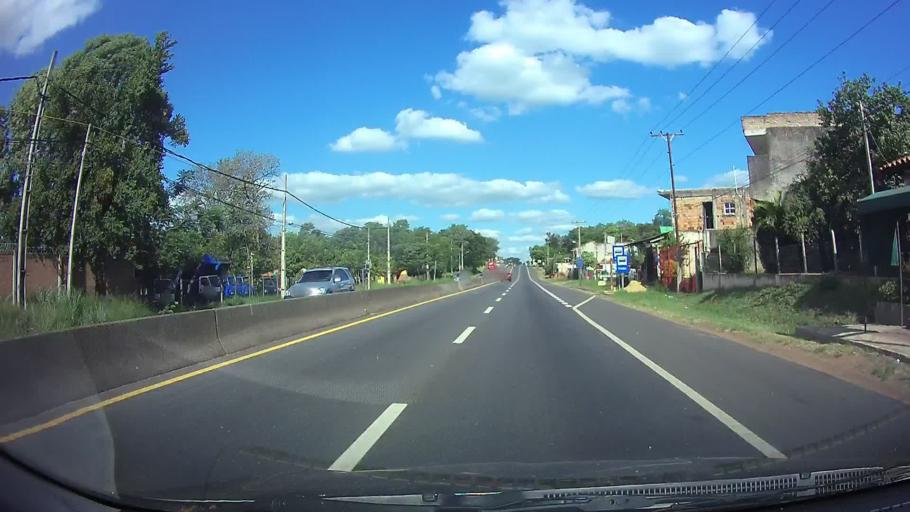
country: PY
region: Central
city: Itaugua
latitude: -25.3981
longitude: -57.3341
